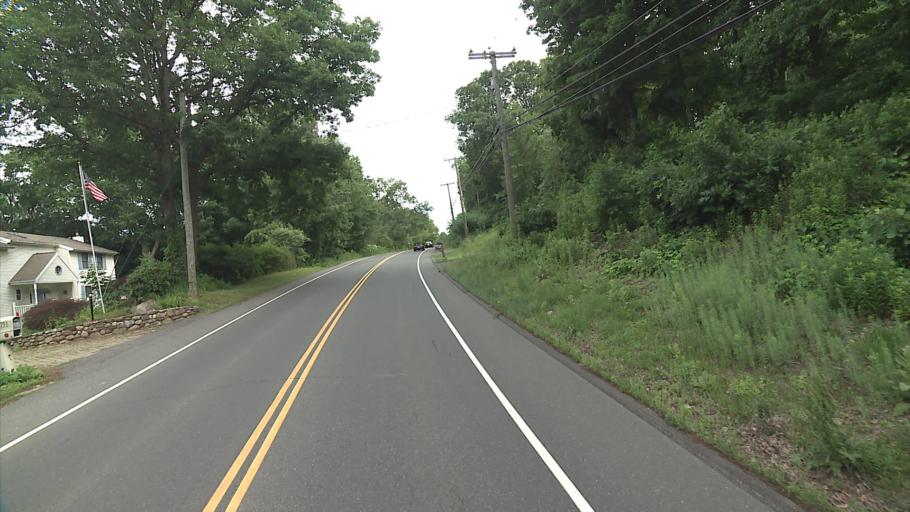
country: US
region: Connecticut
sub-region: Litchfield County
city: Watertown
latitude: 41.6260
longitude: -73.1359
